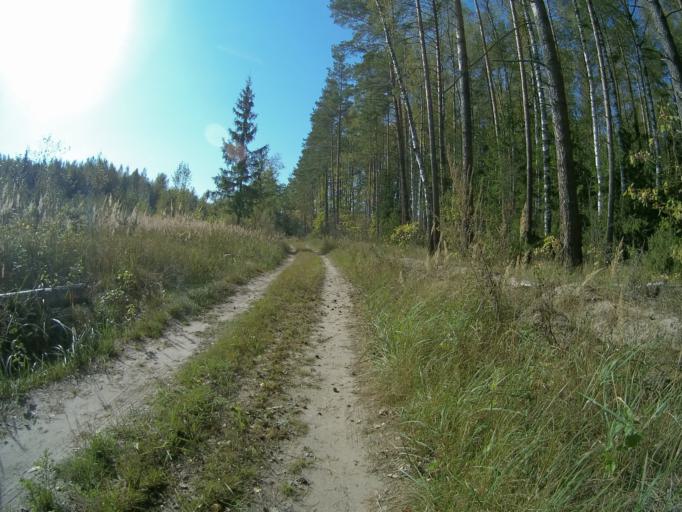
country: RU
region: Vladimir
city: Vorsha
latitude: 55.9735
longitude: 40.1368
